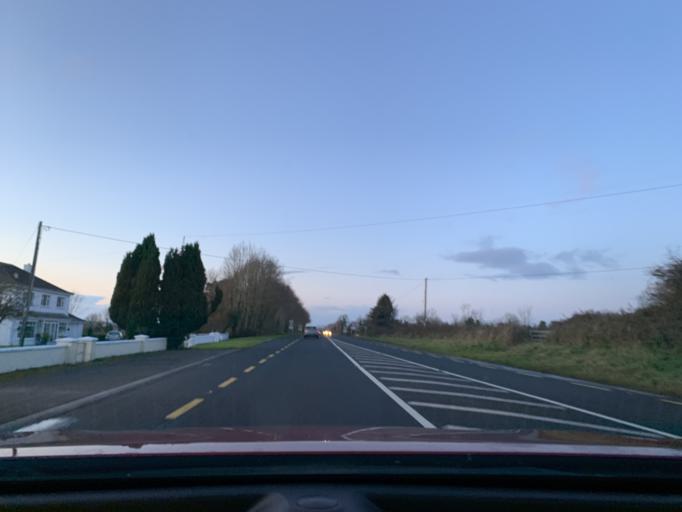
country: IE
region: Connaught
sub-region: County Leitrim
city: Carrick-on-Shannon
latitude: 53.8971
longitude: -7.9524
